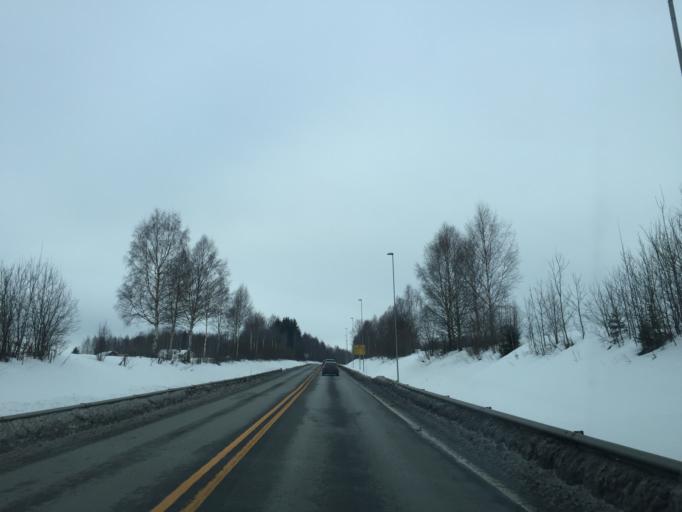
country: NO
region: Hedmark
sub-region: Loten
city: Loten
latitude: 60.7908
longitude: 11.2980
